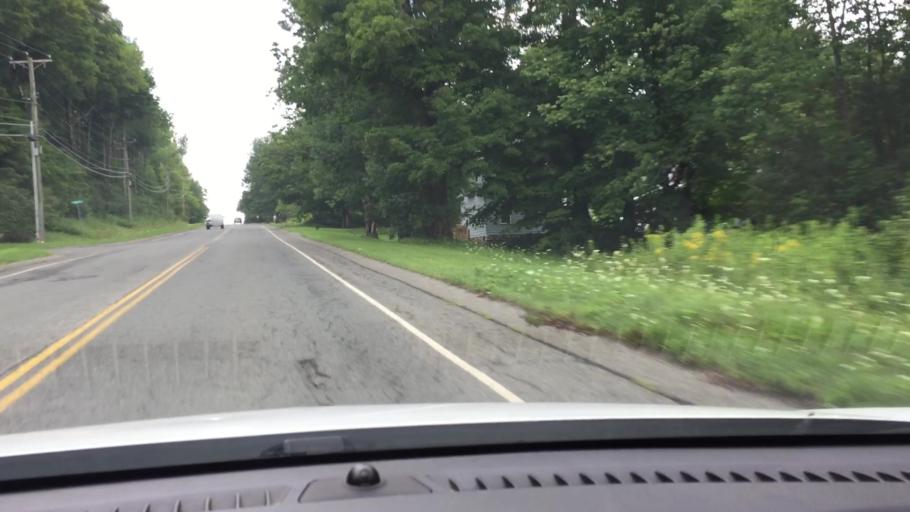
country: US
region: Massachusetts
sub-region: Berkshire County
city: Hinsdale
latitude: 42.4430
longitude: -73.0914
